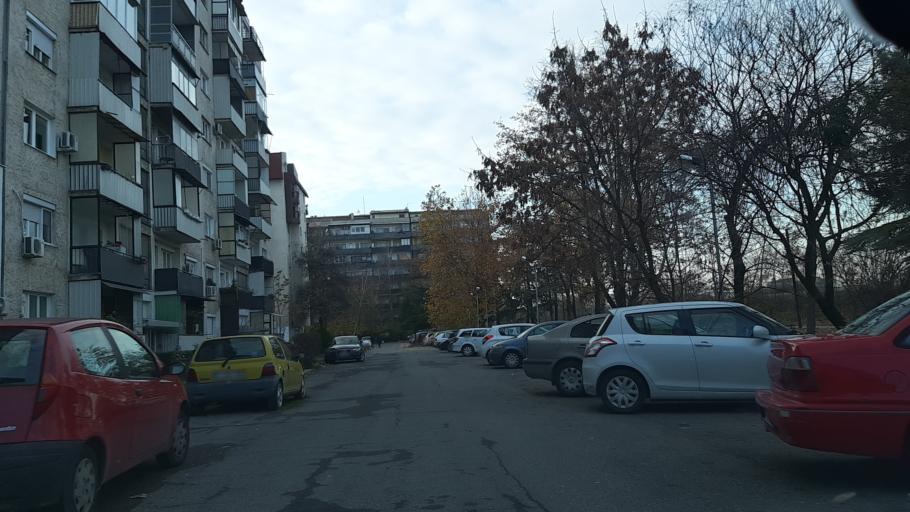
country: MK
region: Karpos
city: Skopje
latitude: 41.9812
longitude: 21.4463
